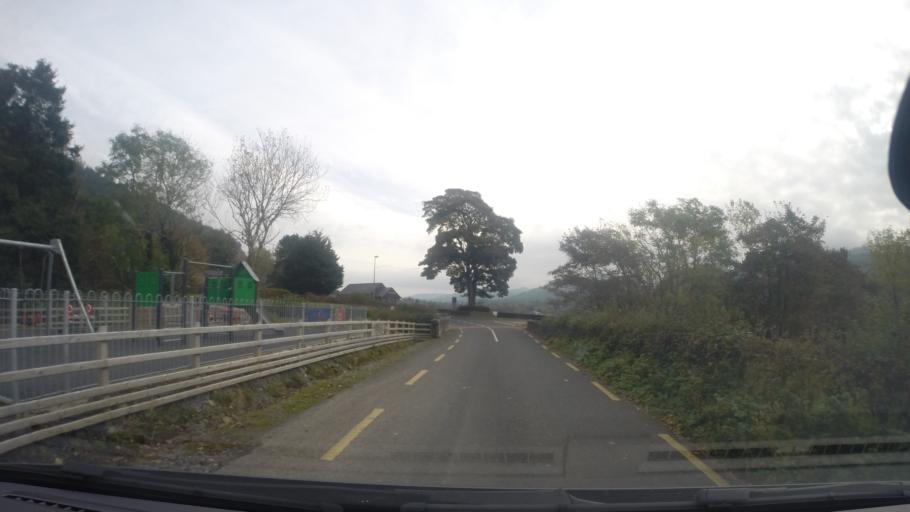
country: IE
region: Connaught
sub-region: Sligo
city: Sligo
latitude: 54.3389
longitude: -8.3701
